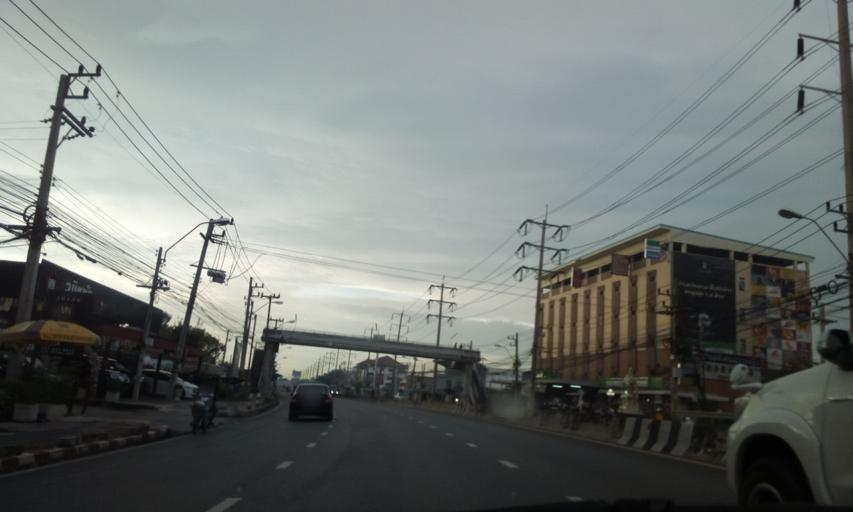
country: TH
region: Phra Nakhon Si Ayutthaya
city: Ban Bang Kadi Pathum Thani
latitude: 13.9572
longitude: 100.5506
